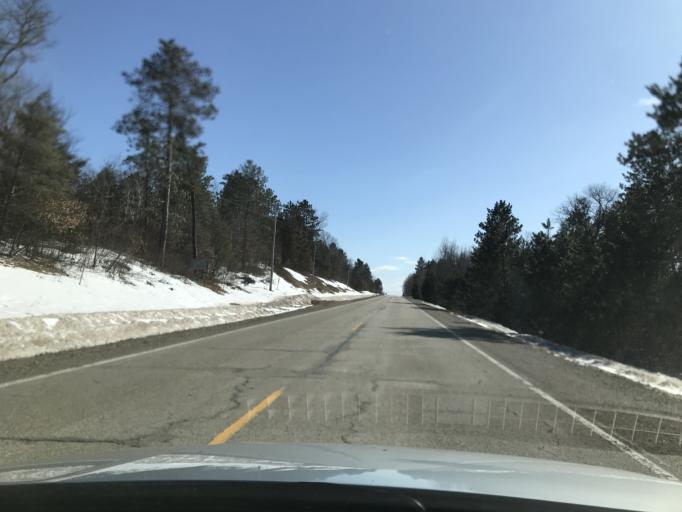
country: US
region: Wisconsin
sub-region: Marinette County
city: Niagara
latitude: 45.3611
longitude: -88.1008
